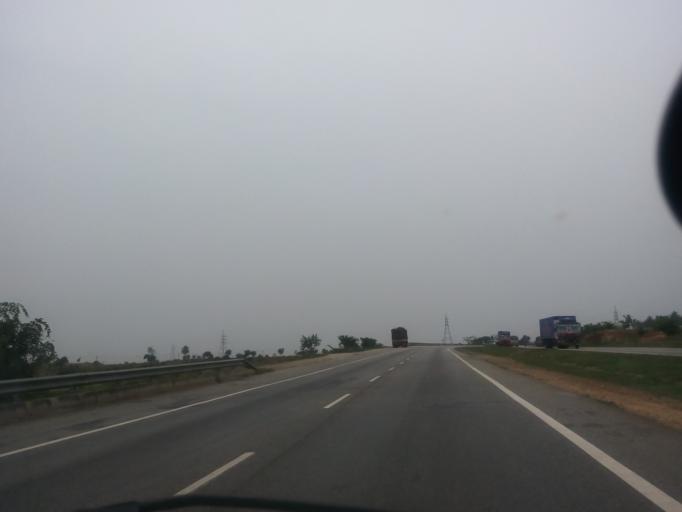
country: IN
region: Karnataka
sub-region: Bangalore Urban
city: Bangalore
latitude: 12.9086
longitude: 77.4681
